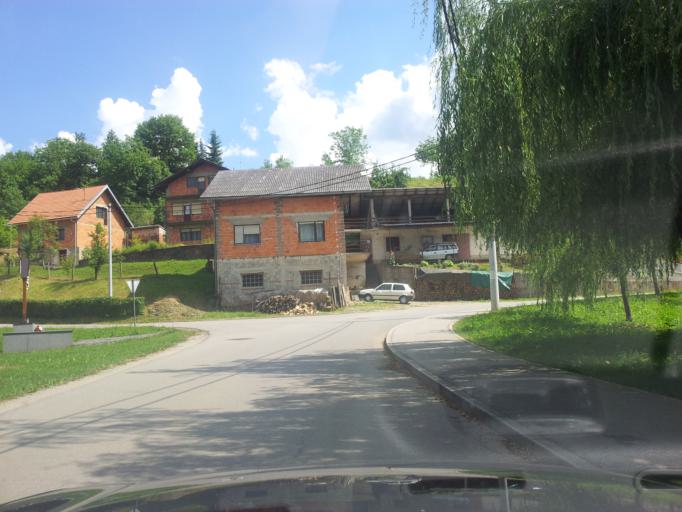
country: HR
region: Karlovacka
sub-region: Grad Karlovac
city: Karlovac
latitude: 45.4506
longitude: 15.5069
